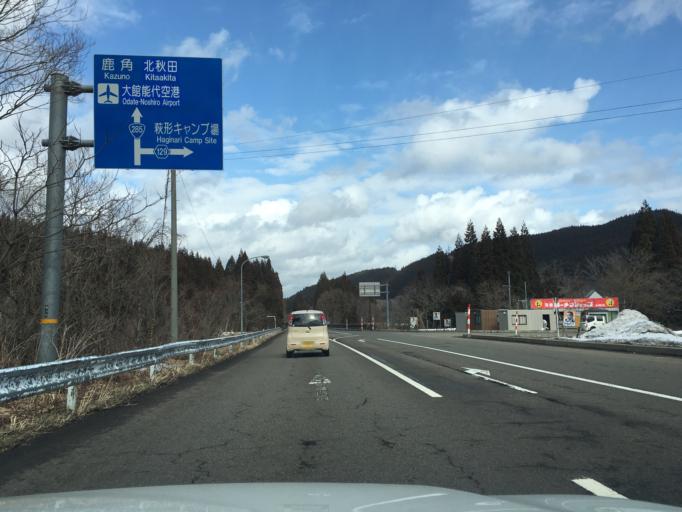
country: JP
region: Akita
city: Takanosu
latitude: 40.0081
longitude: 140.2786
